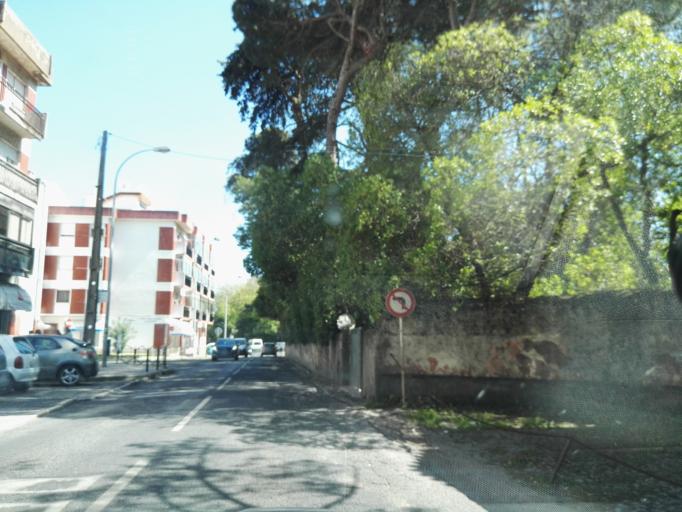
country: PT
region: Lisbon
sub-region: Sintra
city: Rio de Mouro
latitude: 38.7943
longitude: -9.3476
